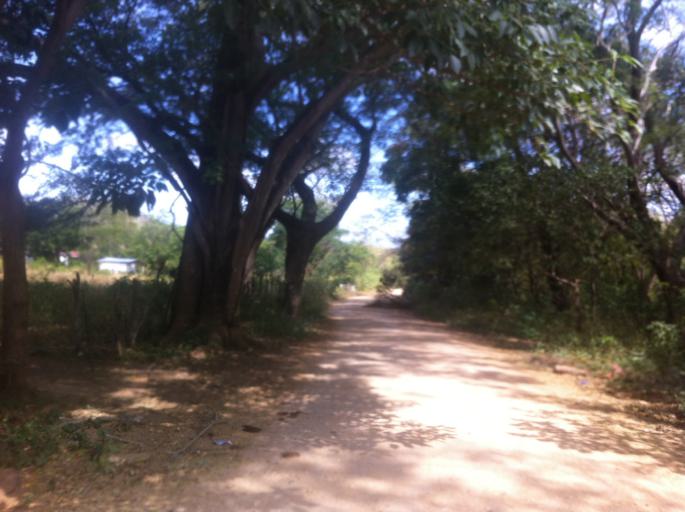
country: NI
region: Rivas
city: Tola
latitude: 11.3953
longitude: -86.0316
